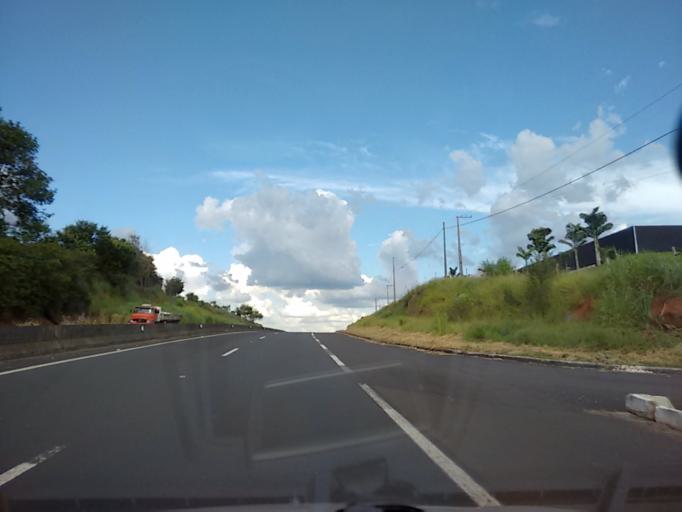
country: BR
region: Sao Paulo
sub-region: Marilia
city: Marilia
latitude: -22.2152
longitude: -49.8441
